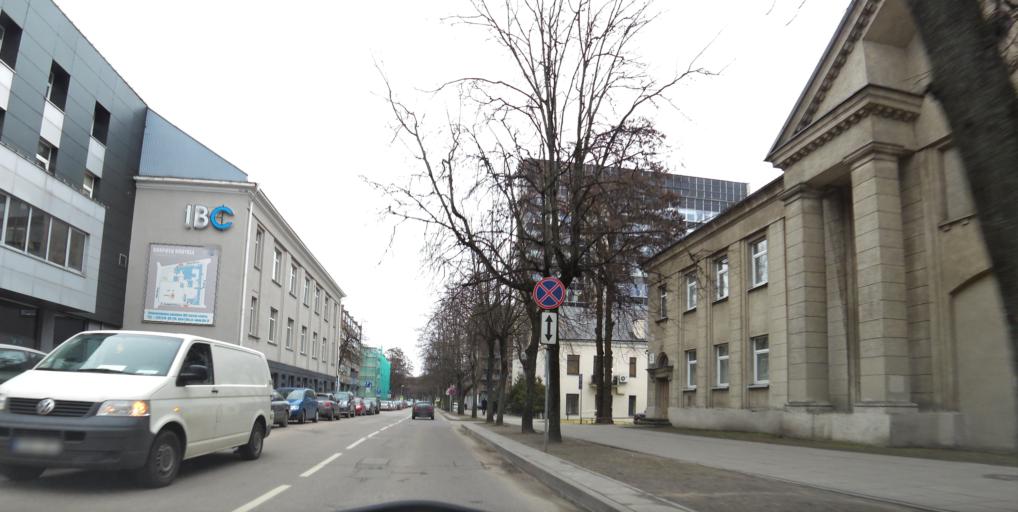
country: LT
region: Vilnius County
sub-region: Vilnius
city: Vilnius
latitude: 54.6930
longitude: 25.2827
